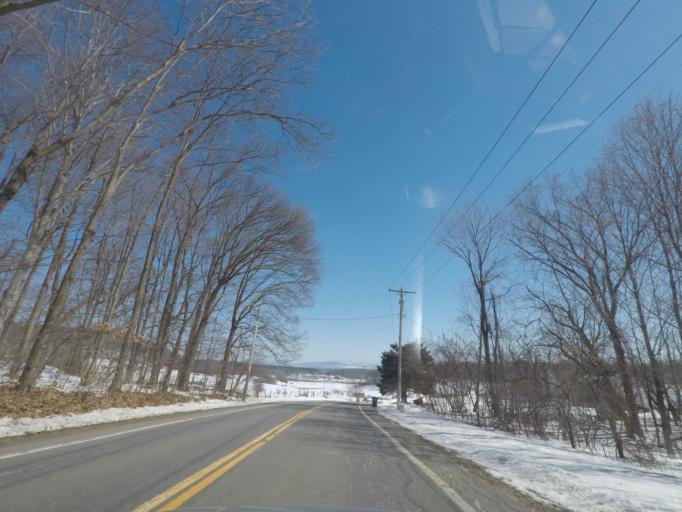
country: US
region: New York
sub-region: Saratoga County
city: Stillwater
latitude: 43.0239
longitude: -73.6688
